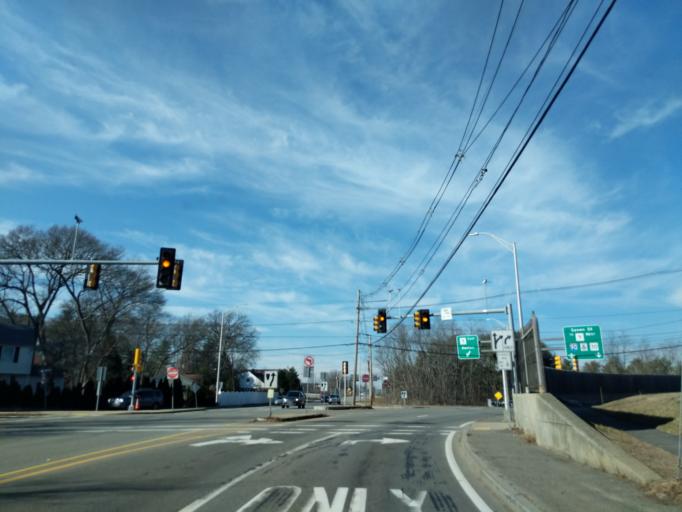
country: US
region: Massachusetts
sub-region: Middlesex County
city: Cochituate
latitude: 42.2973
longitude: -71.3777
